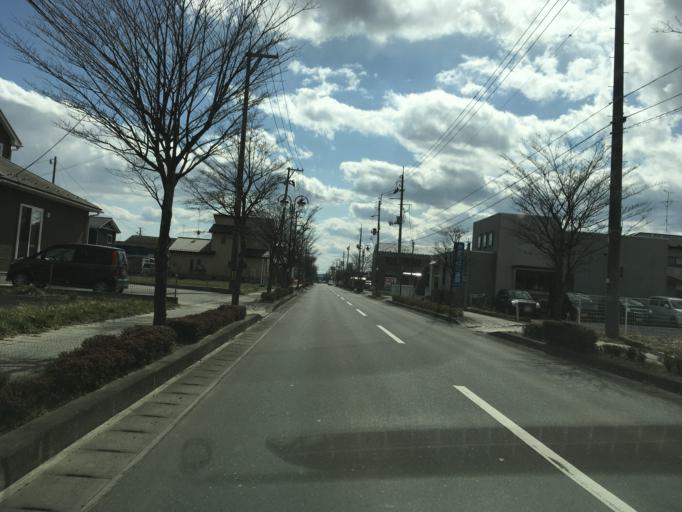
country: JP
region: Miyagi
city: Wakuya
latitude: 38.7049
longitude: 141.2144
